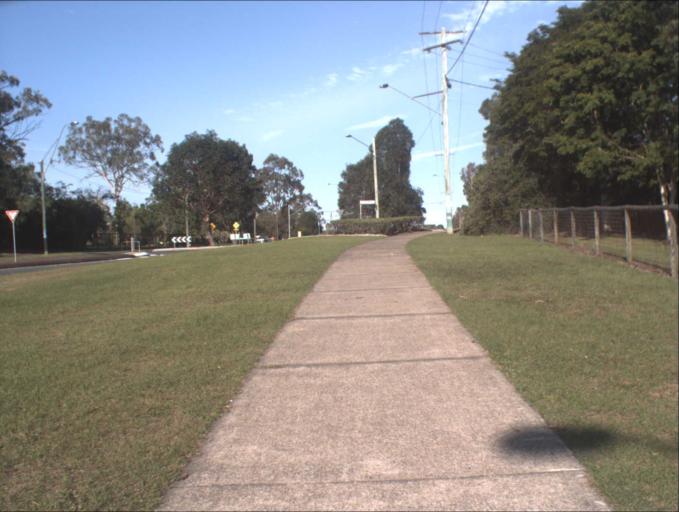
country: AU
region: Queensland
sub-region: Logan
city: Park Ridge South
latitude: -27.6988
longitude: 153.0329
